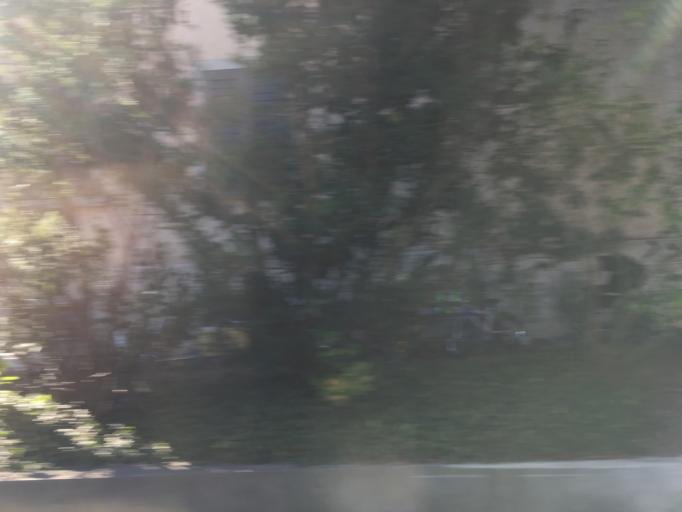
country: CH
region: Zurich
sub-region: Bezirk Hinwil
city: Baretswil
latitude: 47.3363
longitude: 8.8535
